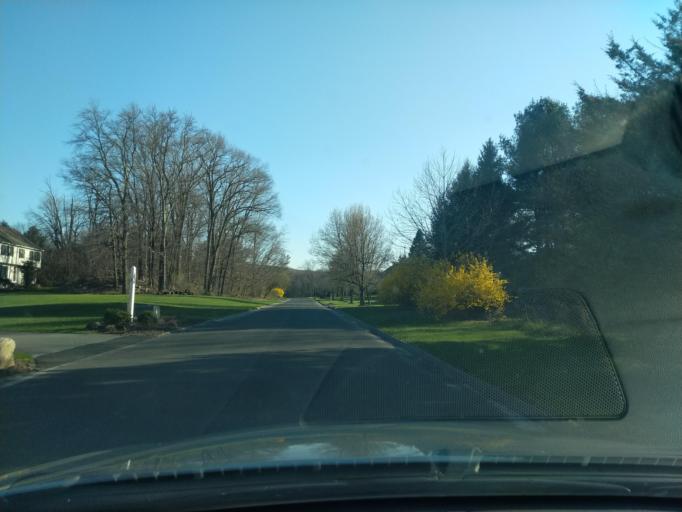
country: US
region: Connecticut
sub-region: Fairfield County
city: Newtown
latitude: 41.3593
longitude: -73.2815
